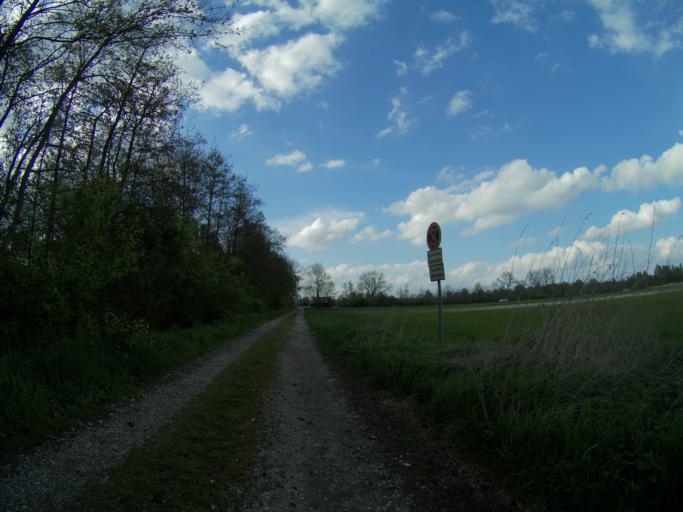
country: DE
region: Bavaria
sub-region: Upper Bavaria
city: Marzling
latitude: 48.3869
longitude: 11.7945
